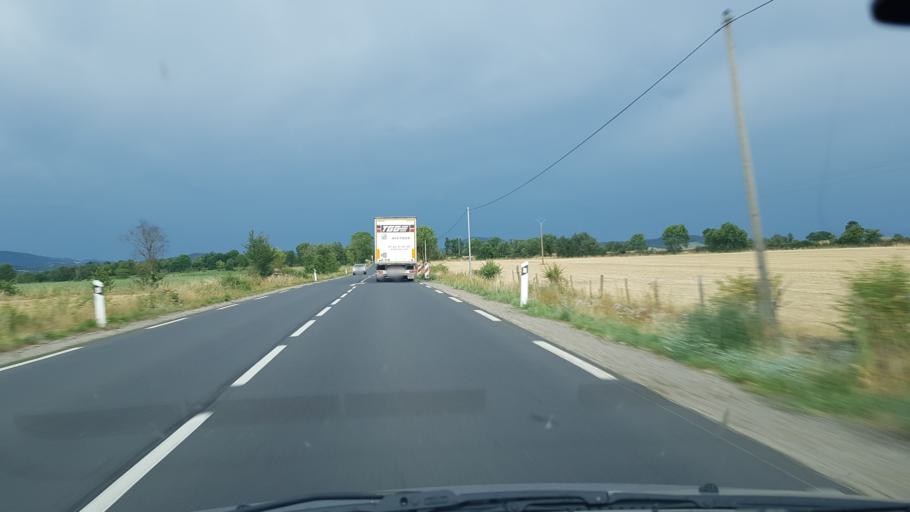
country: FR
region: Auvergne
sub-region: Departement de la Haute-Loire
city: Paulhaguet
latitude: 45.1679
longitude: 3.5289
